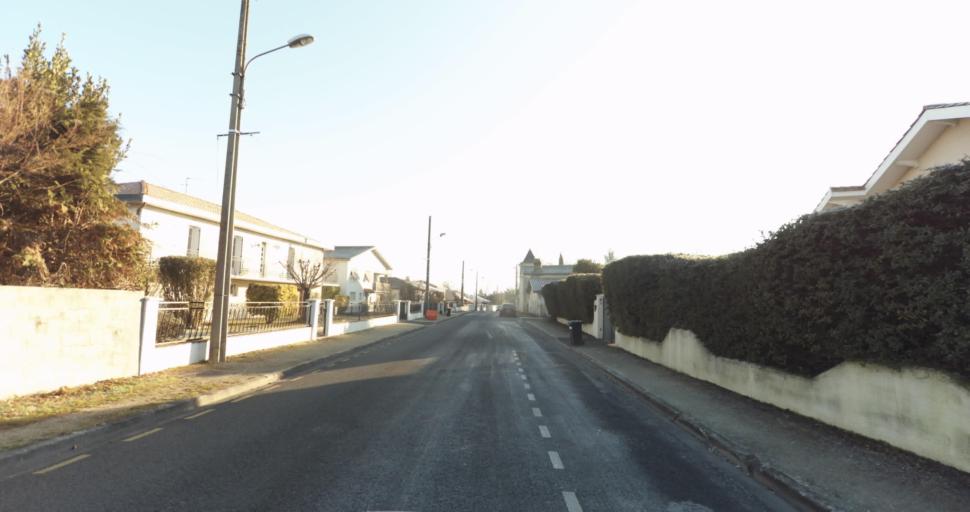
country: FR
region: Aquitaine
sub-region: Departement de la Gironde
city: Carbon-Blanc
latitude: 44.9058
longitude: -0.5029
